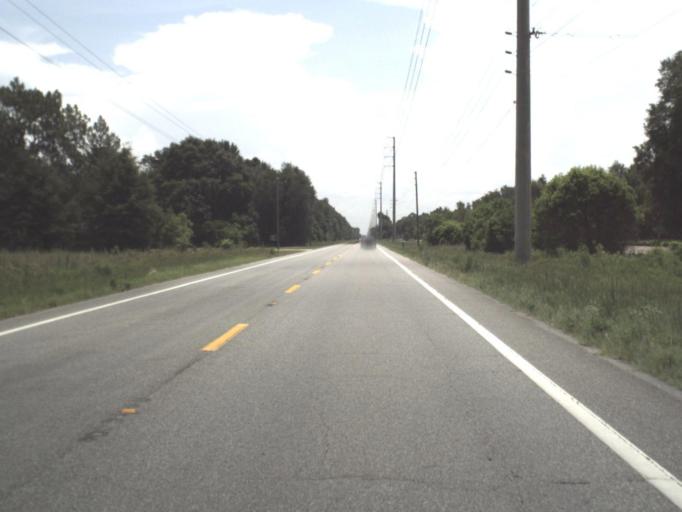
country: US
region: Florida
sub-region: Madison County
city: Madison
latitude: 30.4133
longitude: -83.2759
